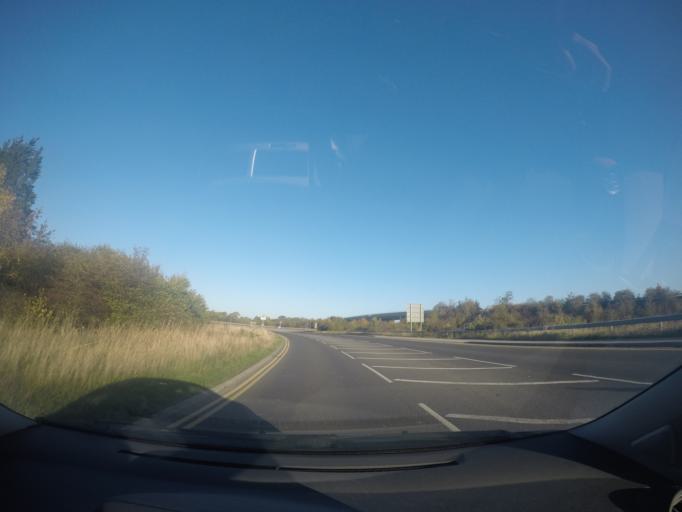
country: GB
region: England
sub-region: City of York
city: Askham Richard
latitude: 53.9066
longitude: -1.1839
